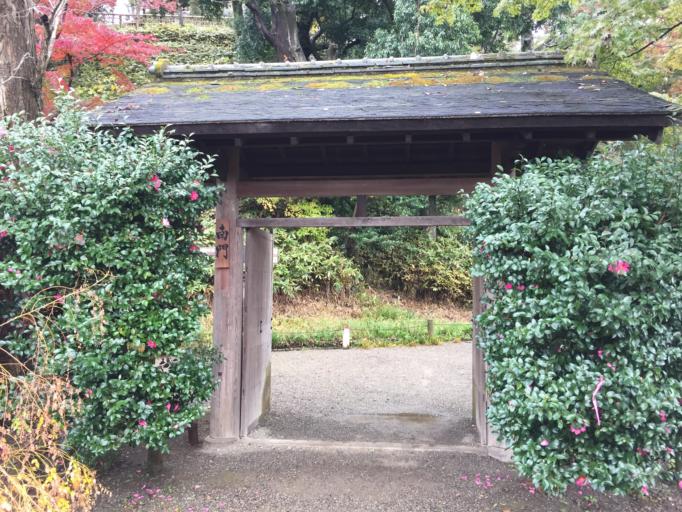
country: JP
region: Ibaraki
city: Mito-shi
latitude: 36.3738
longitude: 140.4521
